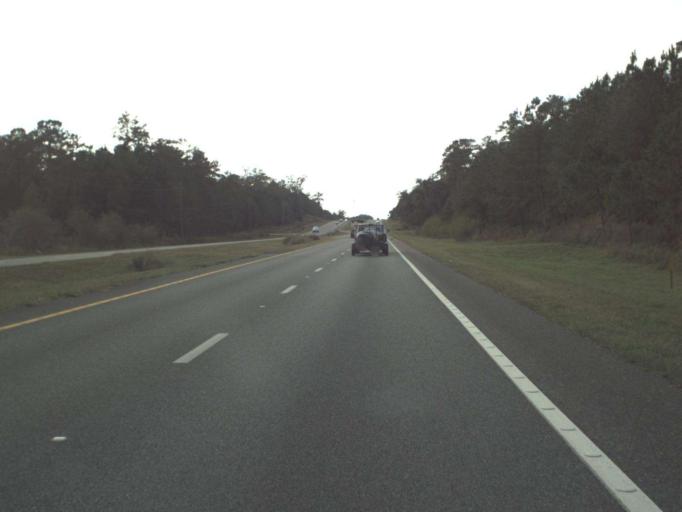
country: US
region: Florida
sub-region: Leon County
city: Tallahassee
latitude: 30.5882
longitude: -84.1941
